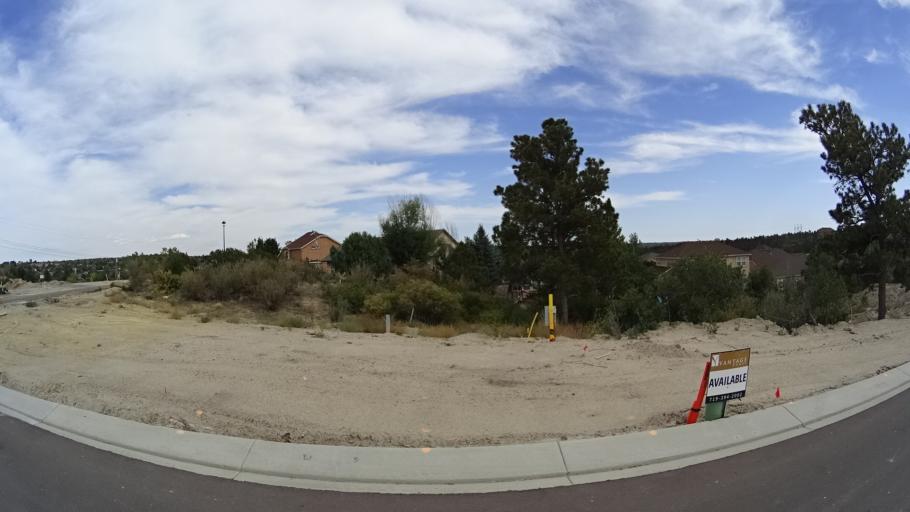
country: US
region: Colorado
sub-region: El Paso County
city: Colorado Springs
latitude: 38.9032
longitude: -104.7873
